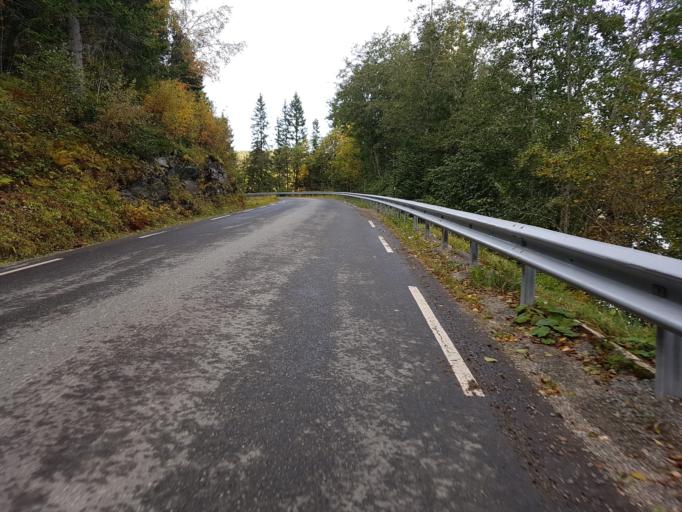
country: NO
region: Sor-Trondelag
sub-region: Klaebu
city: Klaebu
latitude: 63.3430
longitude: 10.5535
